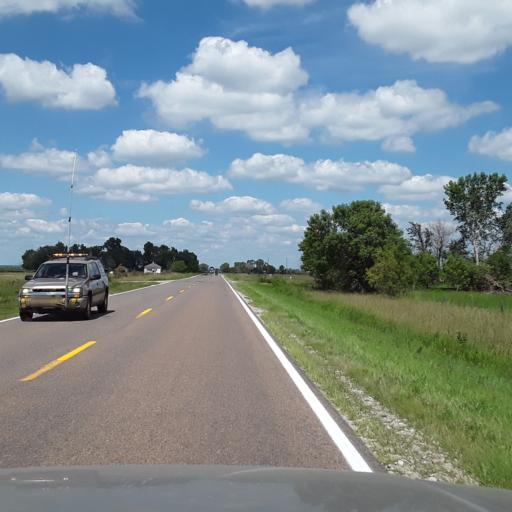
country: US
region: Nebraska
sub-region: Nance County
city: Genoa
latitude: 41.3653
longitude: -97.6947
